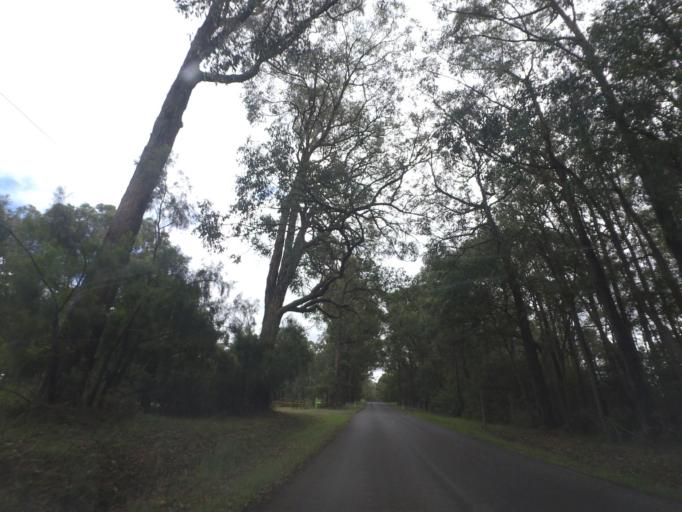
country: AU
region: Victoria
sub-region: Yarra Ranges
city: Launching Place
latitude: -37.8168
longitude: 145.5755
